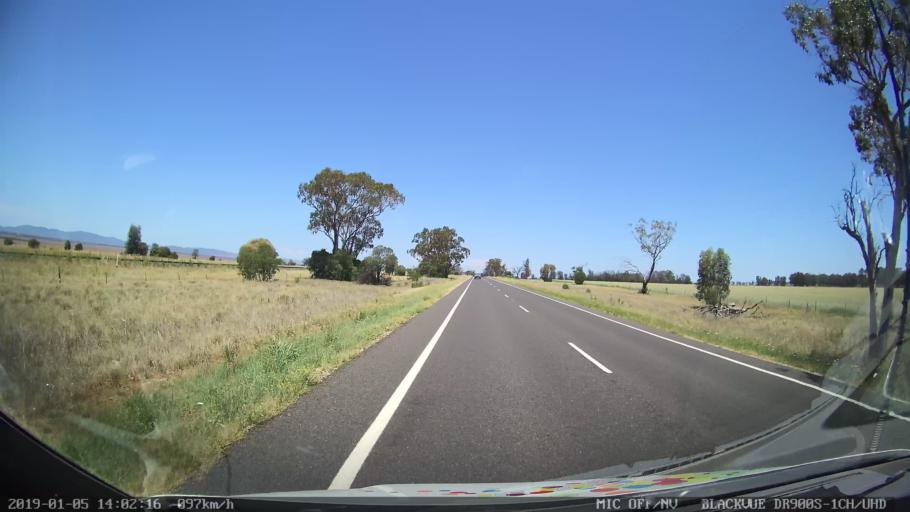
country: AU
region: New South Wales
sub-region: Gunnedah
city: Gunnedah
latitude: -31.1780
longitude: 150.3357
